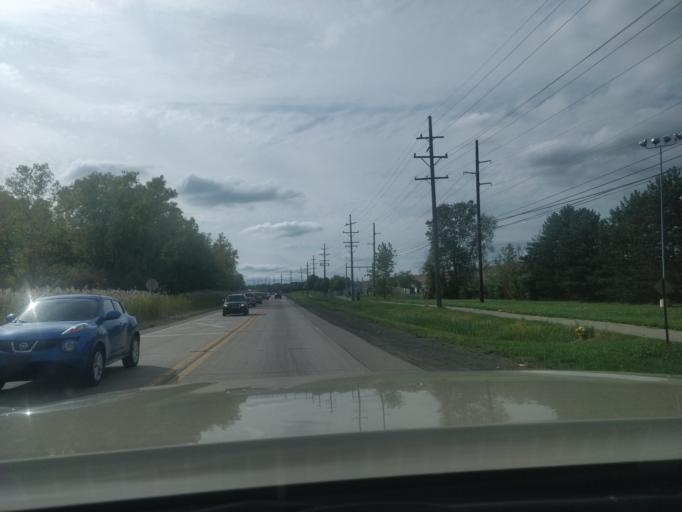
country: US
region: Michigan
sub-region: Wayne County
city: Woodhaven
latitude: 42.1551
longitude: -83.2329
